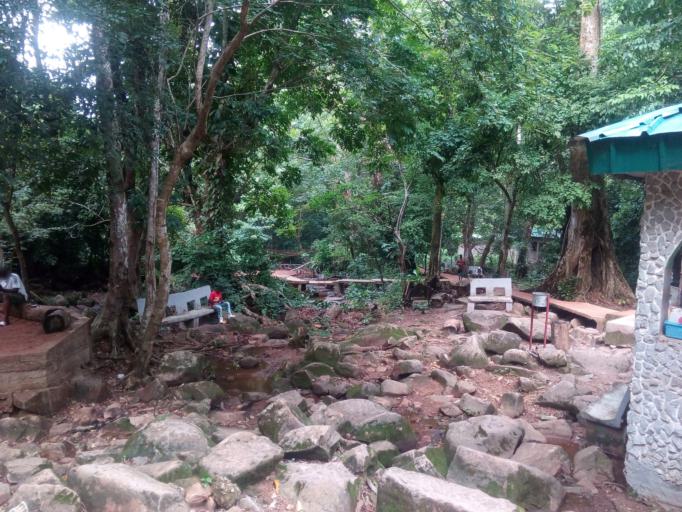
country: CI
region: Dix-Huit Montagnes
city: Man
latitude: 7.4120
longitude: -7.5861
